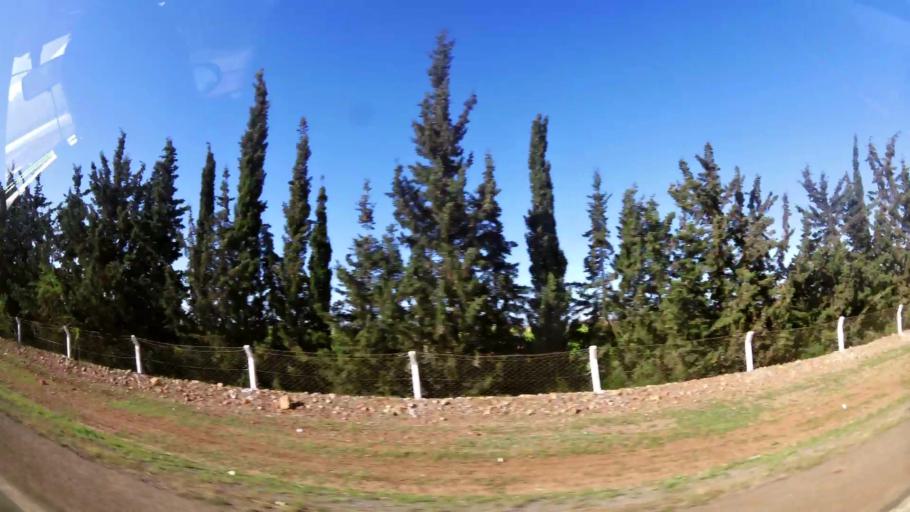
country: MA
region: Oriental
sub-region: Berkane-Taourirt
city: Ahfir
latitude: 35.0024
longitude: -2.1790
